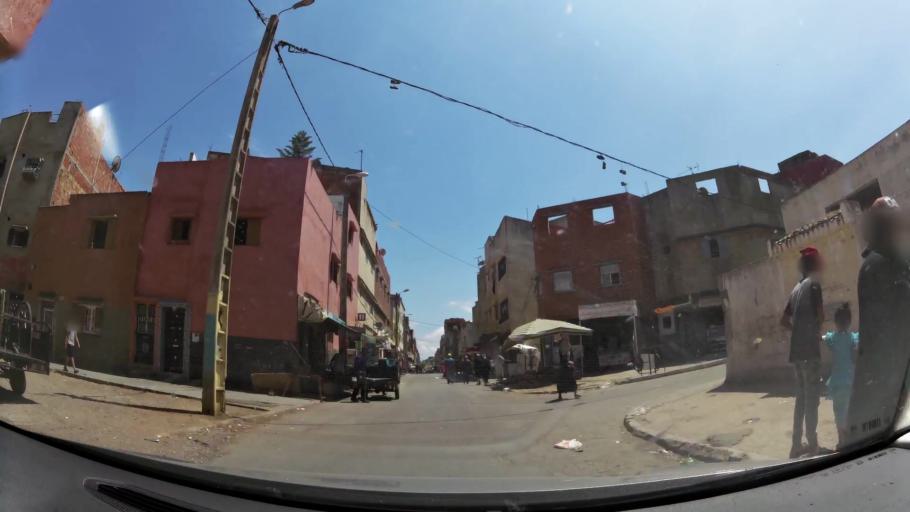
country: MA
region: Gharb-Chrarda-Beni Hssen
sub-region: Kenitra Province
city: Kenitra
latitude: 34.2527
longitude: -6.5551
